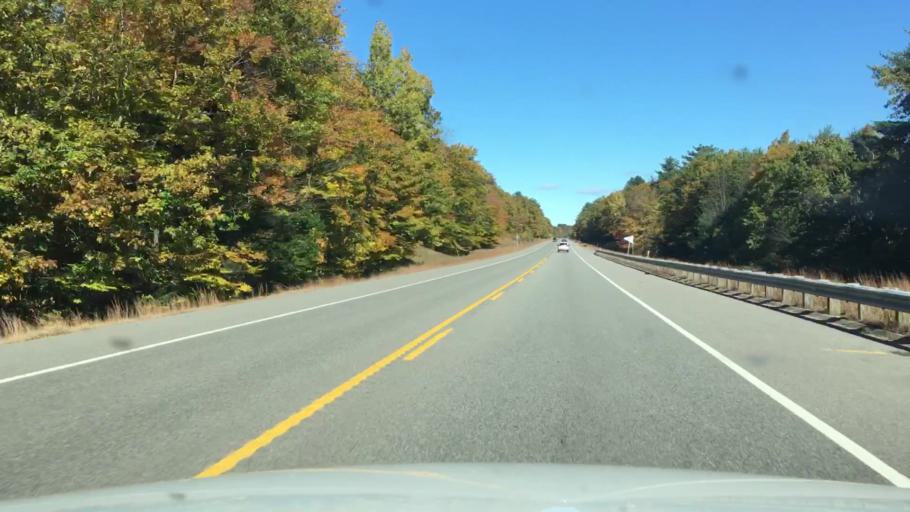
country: US
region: New Hampshire
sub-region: Carroll County
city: Sanbornville
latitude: 43.5051
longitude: -71.0292
